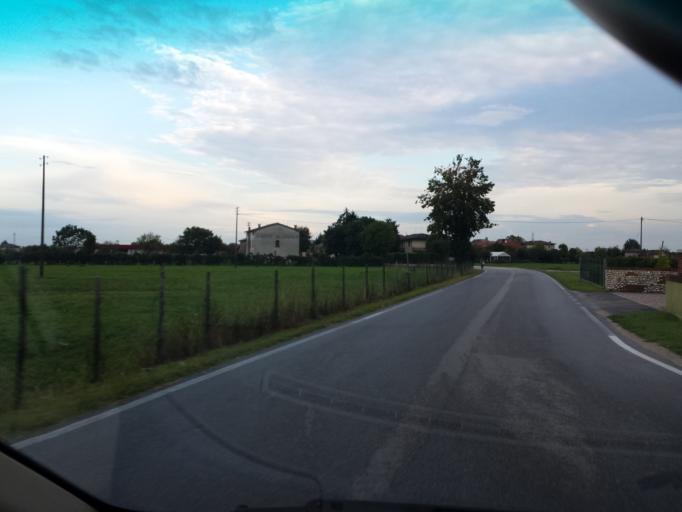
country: IT
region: Veneto
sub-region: Provincia di Vicenza
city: Sandrigo
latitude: 45.6535
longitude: 11.5930
